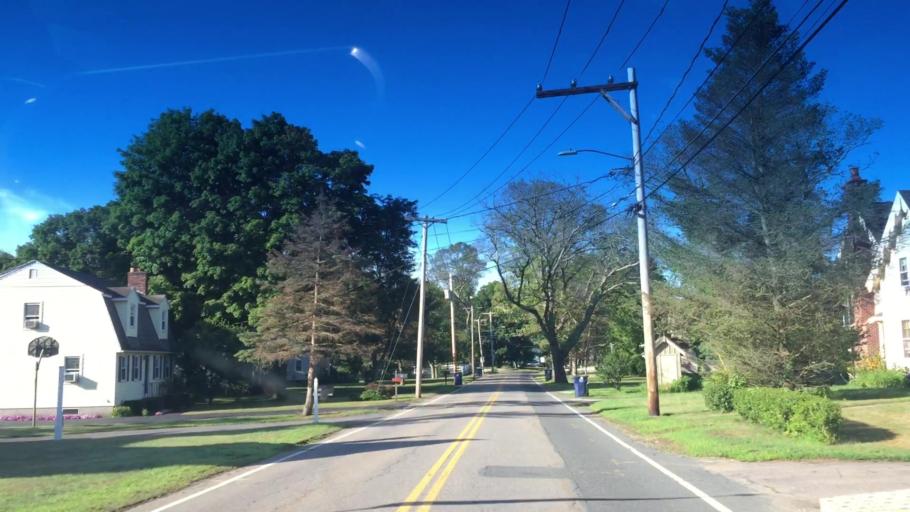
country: US
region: Massachusetts
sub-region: Norfolk County
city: Medway
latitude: 42.1449
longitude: -71.3916
